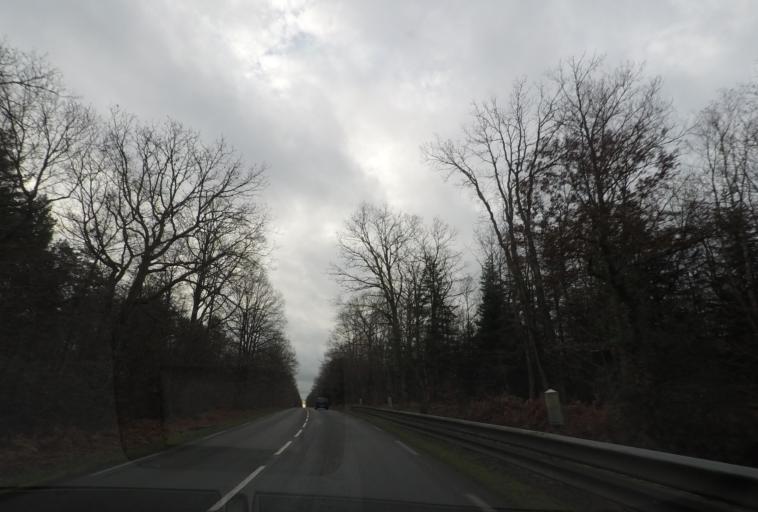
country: FR
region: Pays de la Loire
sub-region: Departement de la Sarthe
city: Vibraye
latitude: 48.0393
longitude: 0.7439
